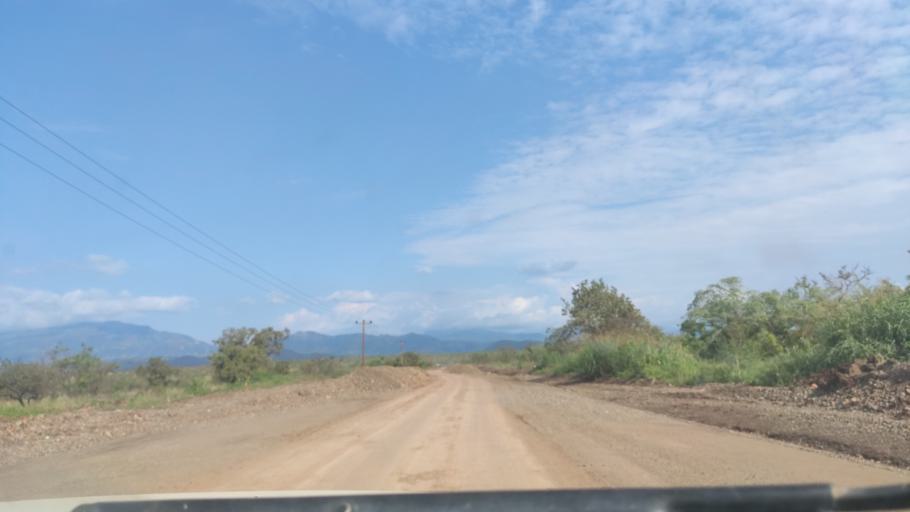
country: ET
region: Southern Nations, Nationalities, and People's Region
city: Felege Neway
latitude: 6.4254
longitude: 37.2321
